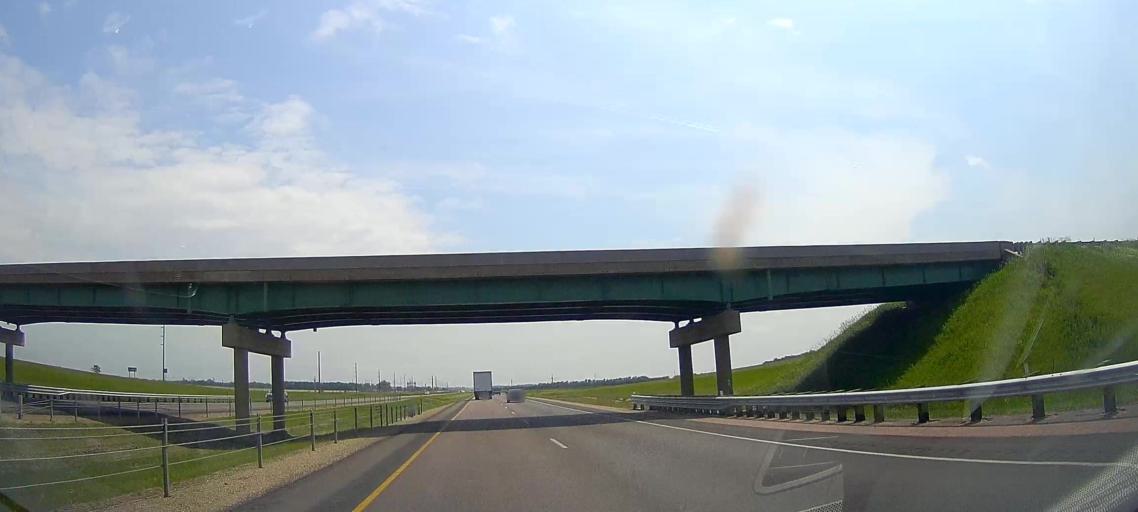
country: US
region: South Dakota
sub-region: Union County
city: Beresford
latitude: 43.1270
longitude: -96.7969
